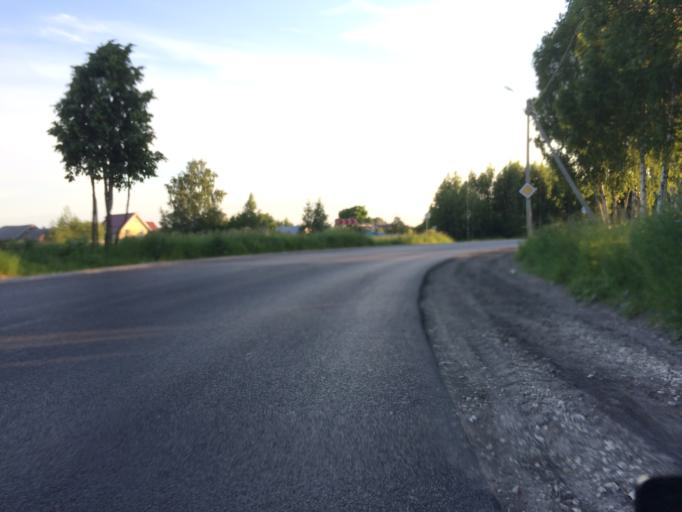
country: RU
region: Mariy-El
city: Medvedevo
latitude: 56.6491
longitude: 47.8307
